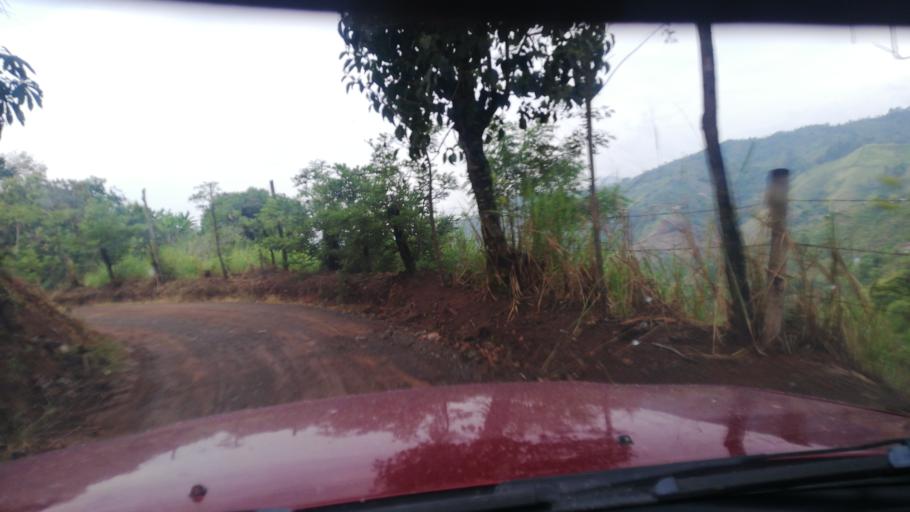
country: CO
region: Risaralda
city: Balboa
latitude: 4.8865
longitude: -75.9510
